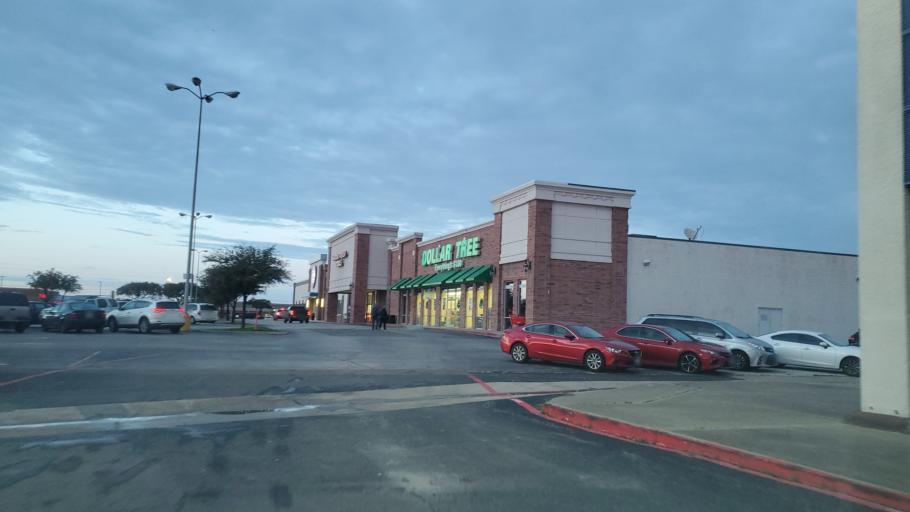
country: US
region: Texas
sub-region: Dallas County
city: Carrollton
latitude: 32.9985
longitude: -96.8852
